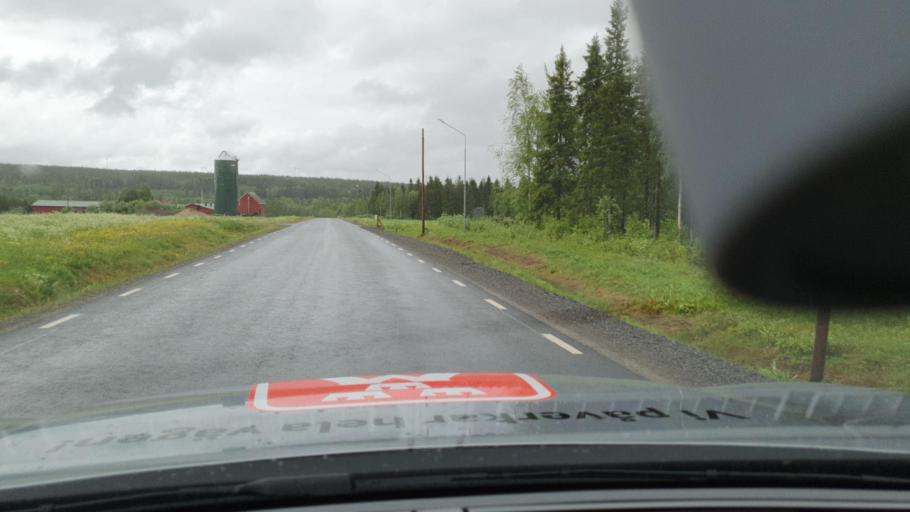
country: FI
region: Lapland
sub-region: Torniolaakso
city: Ylitornio
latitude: 66.1889
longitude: 23.7147
